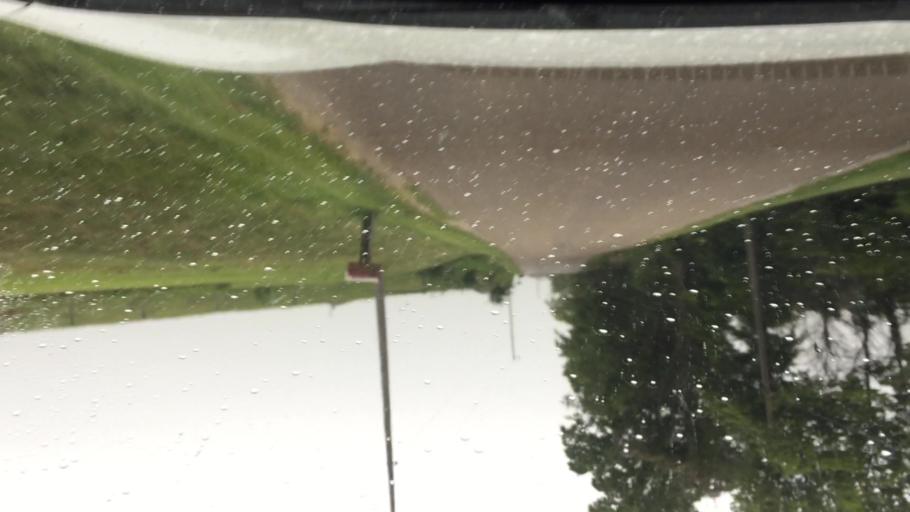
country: US
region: Ohio
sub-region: Champaign County
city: Mechanicsburg
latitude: 40.0166
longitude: -83.6359
